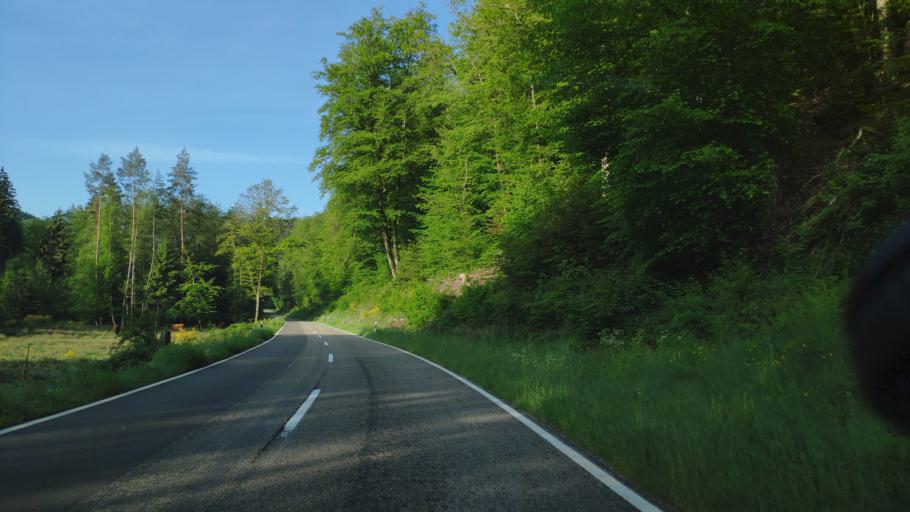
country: DE
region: Rheinland-Pfalz
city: Hinterweidenthal
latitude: 49.1886
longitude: 7.7245
